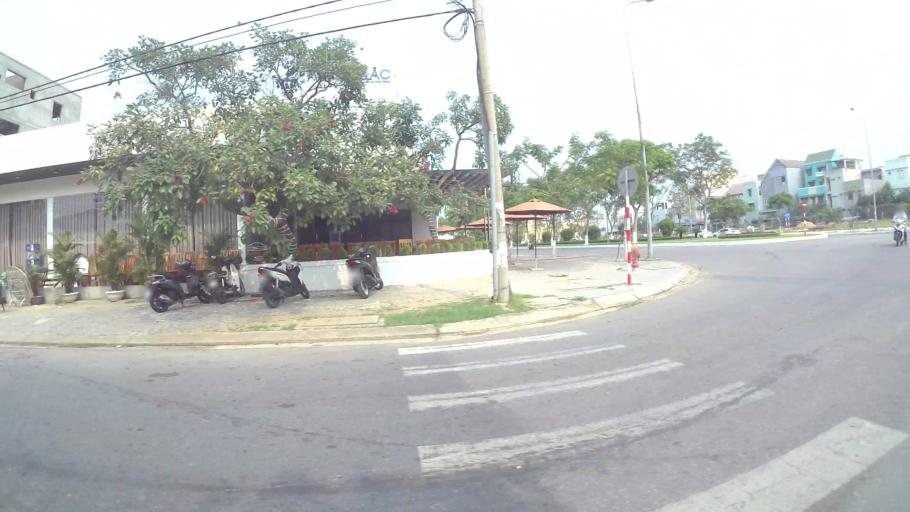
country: VN
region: Da Nang
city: Cam Le
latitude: 16.0401
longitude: 108.2137
